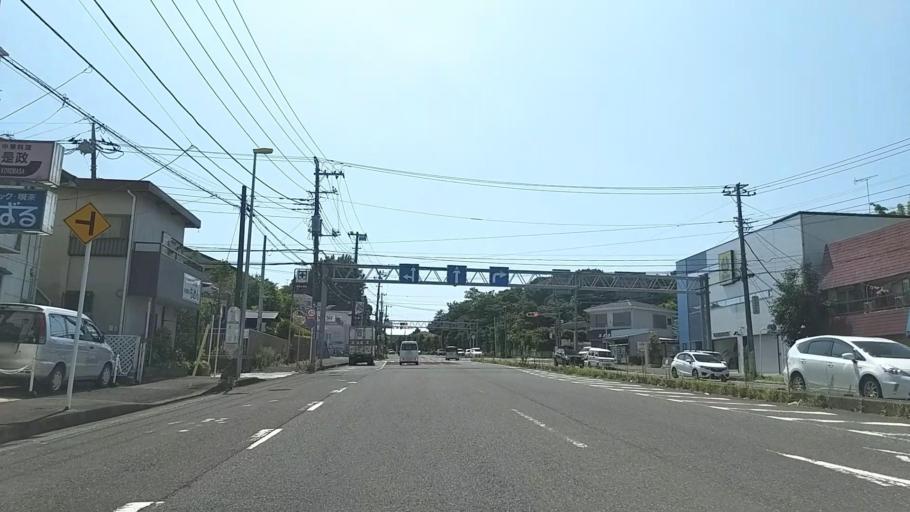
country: JP
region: Kanagawa
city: Fujisawa
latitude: 35.3584
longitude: 139.5075
